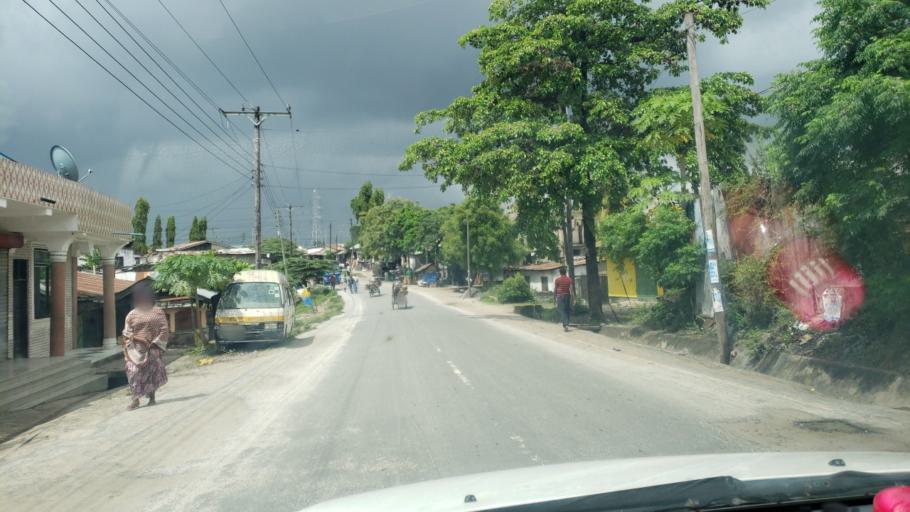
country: TZ
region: Dar es Salaam
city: Magomeni
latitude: -6.8075
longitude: 39.2418
